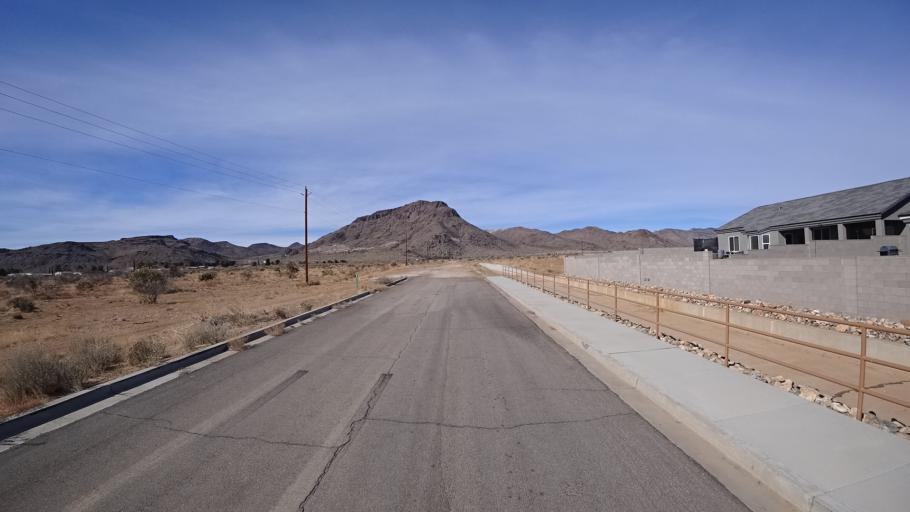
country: US
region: Arizona
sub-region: Mohave County
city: New Kingman-Butler
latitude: 35.2759
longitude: -114.0380
